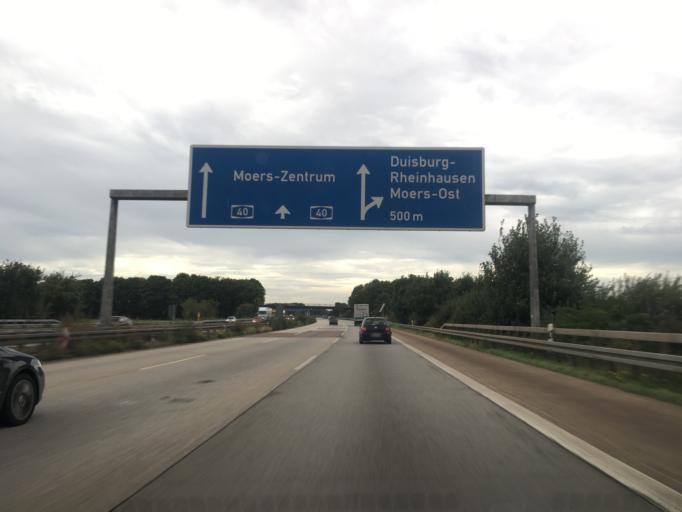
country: DE
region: North Rhine-Westphalia
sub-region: Regierungsbezirk Dusseldorf
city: Moers
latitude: 51.4368
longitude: 6.6897
